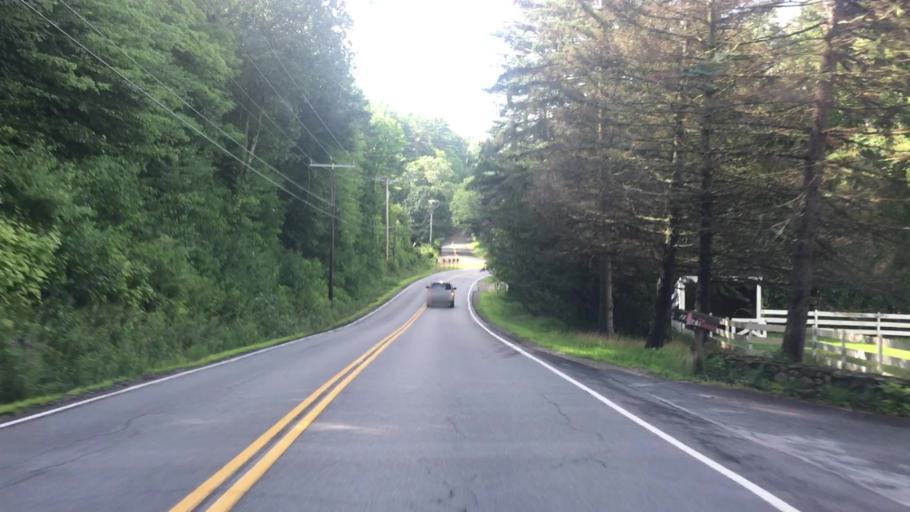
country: US
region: New Hampshire
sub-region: Belknap County
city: Gilford
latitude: 43.5591
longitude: -71.3952
